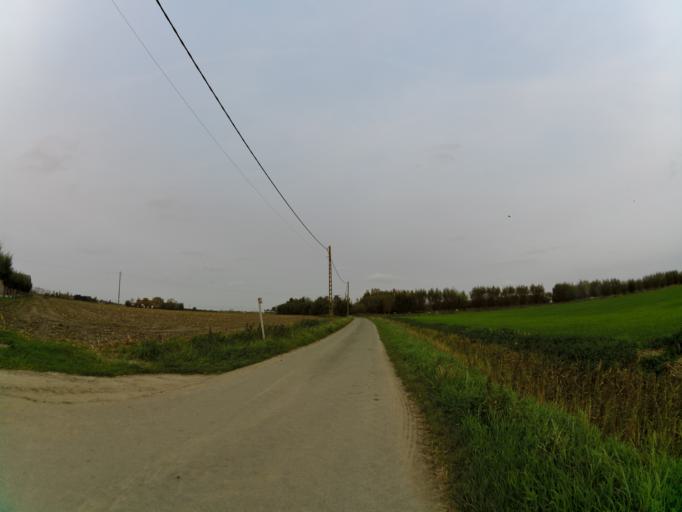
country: BE
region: Flanders
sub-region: Provincie West-Vlaanderen
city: Oudenburg
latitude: 51.2059
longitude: 3.0421
